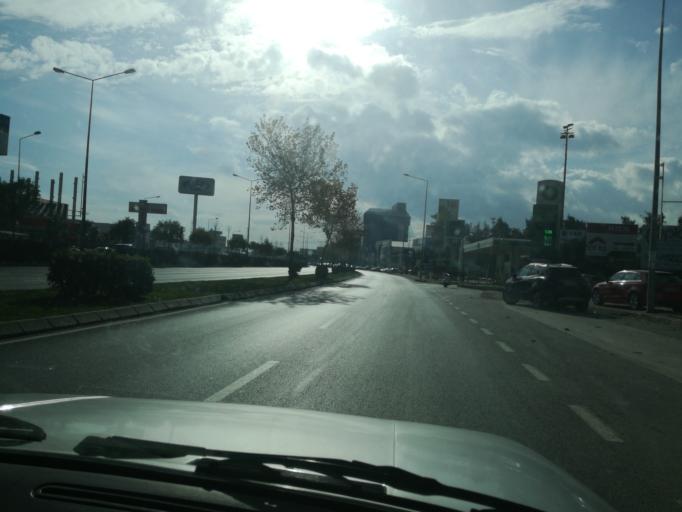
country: TR
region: Izmir
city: Karabaglar
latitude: 38.3556
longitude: 27.1341
